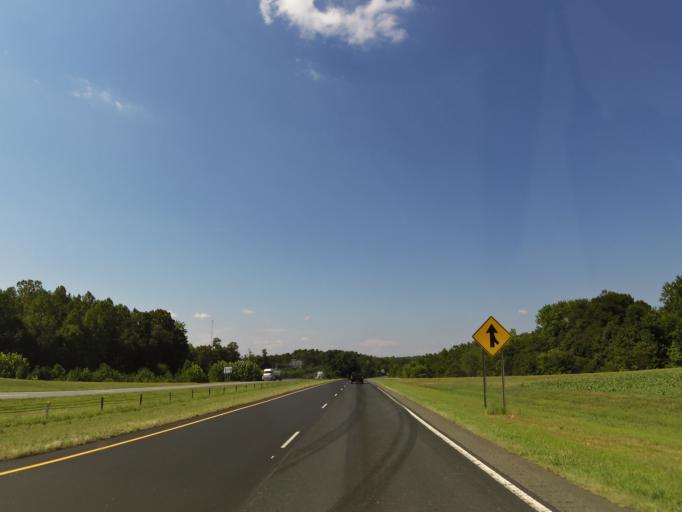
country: US
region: North Carolina
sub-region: Lincoln County
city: Lincolnton
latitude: 35.4797
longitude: -81.2303
